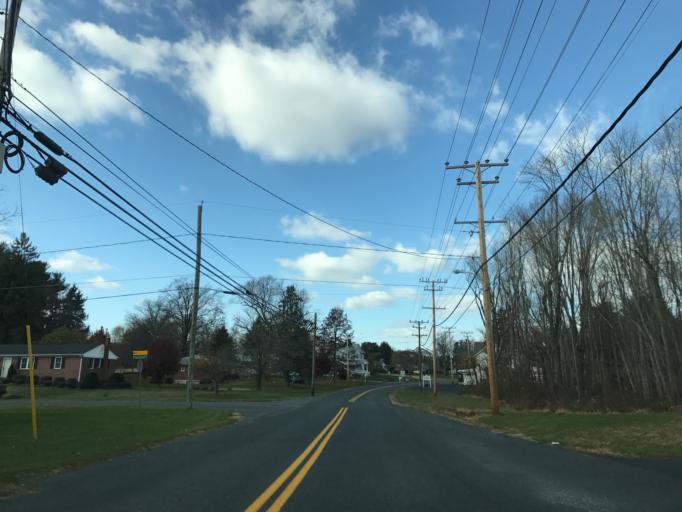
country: US
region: Maryland
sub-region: Harford County
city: Fallston
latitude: 39.5063
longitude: -76.4041
